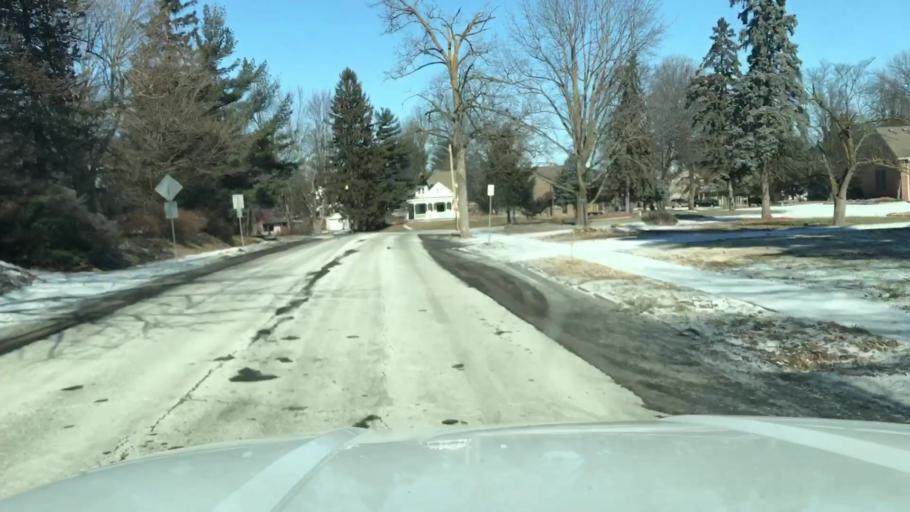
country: US
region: Missouri
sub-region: Andrew County
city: Country Club Village
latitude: 39.7972
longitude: -94.8194
